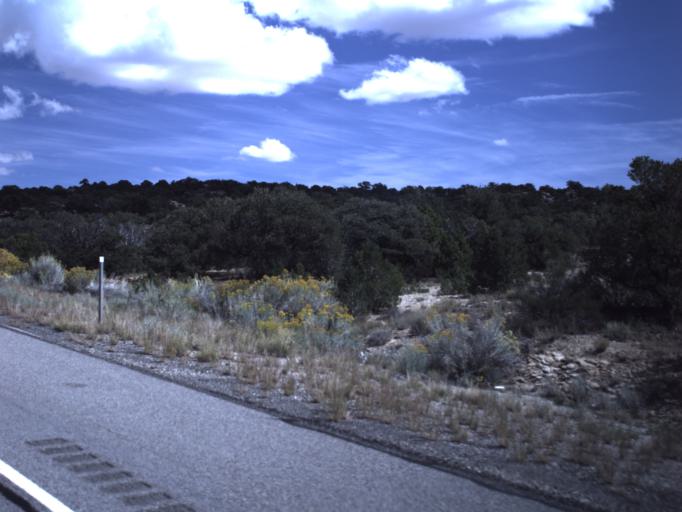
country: US
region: Utah
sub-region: Emery County
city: Ferron
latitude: 38.8634
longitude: -110.8543
